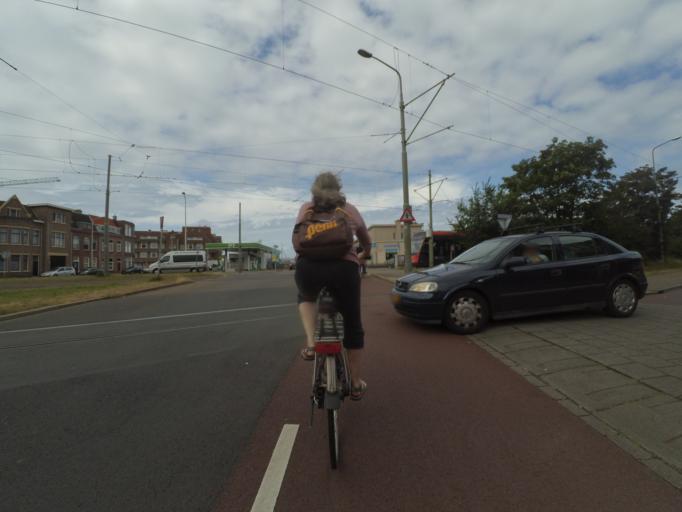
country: NL
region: South Holland
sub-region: Gemeente Den Haag
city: Scheveningen
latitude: 52.0962
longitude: 4.2717
